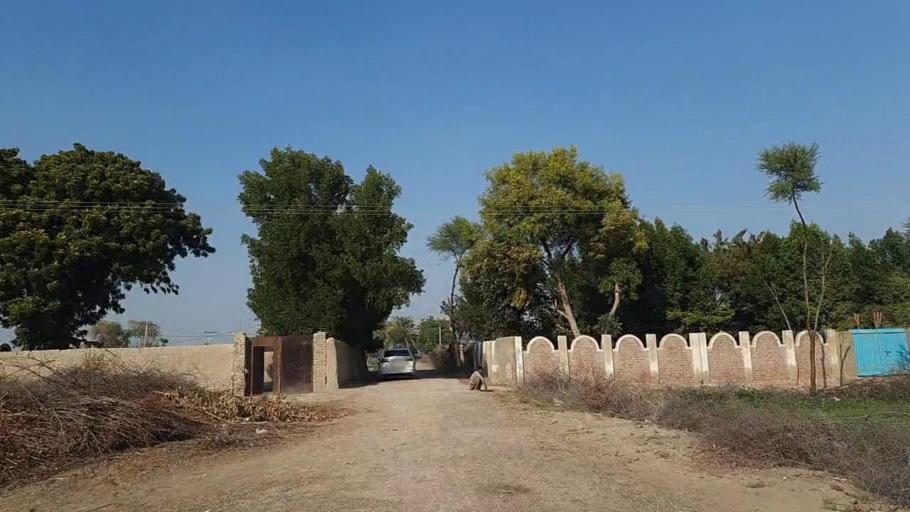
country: PK
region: Sindh
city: Daur
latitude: 26.3576
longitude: 68.3471
